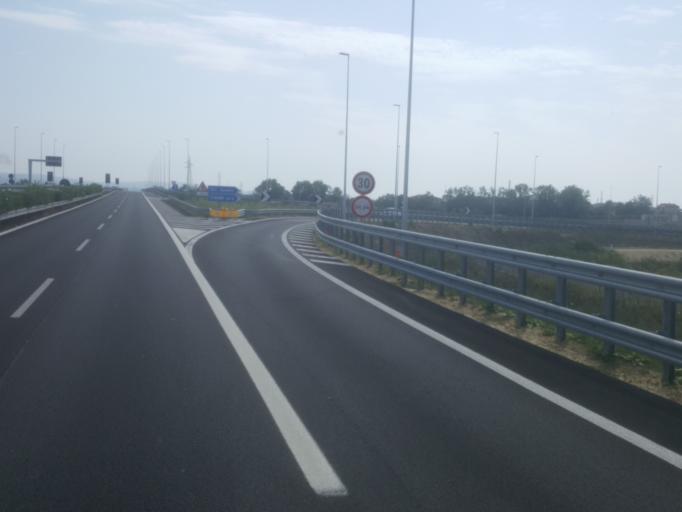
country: IT
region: Tuscany
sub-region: Provincia di Livorno
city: Guasticce
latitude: 43.6066
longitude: 10.3568
